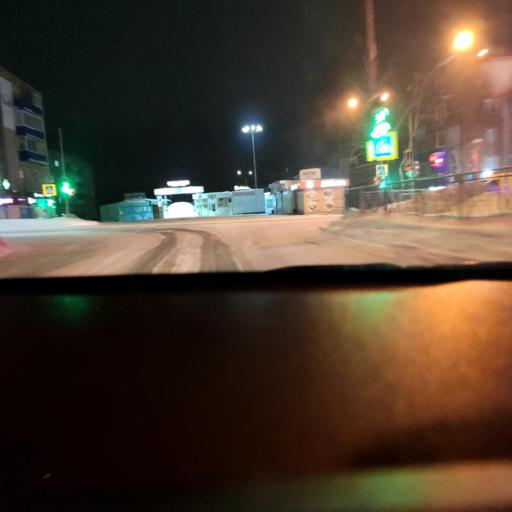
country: RU
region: Tatarstan
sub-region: Chistopol'skiy Rayon
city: Chistopol'
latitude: 55.3659
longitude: 50.6082
